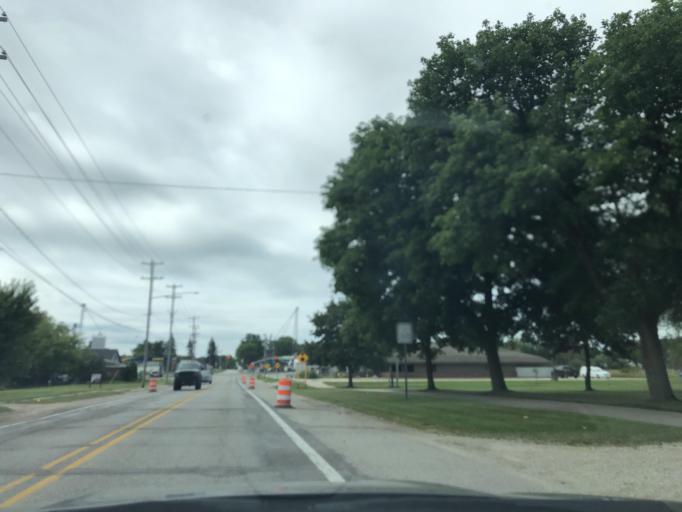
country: US
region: Michigan
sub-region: Missaukee County
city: Lake City
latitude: 44.1957
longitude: -85.2138
